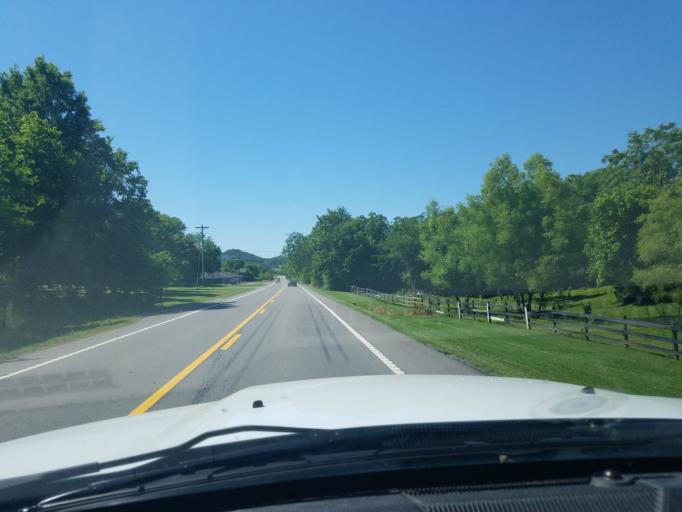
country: US
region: Tennessee
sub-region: Sumner County
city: Westmoreland
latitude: 36.4641
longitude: -86.2695
